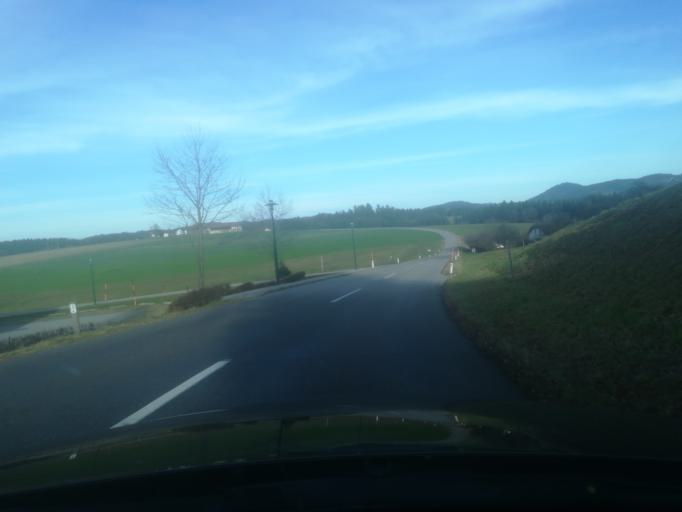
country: AT
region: Upper Austria
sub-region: Politischer Bezirk Perg
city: Perg
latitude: 48.3072
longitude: 14.6595
